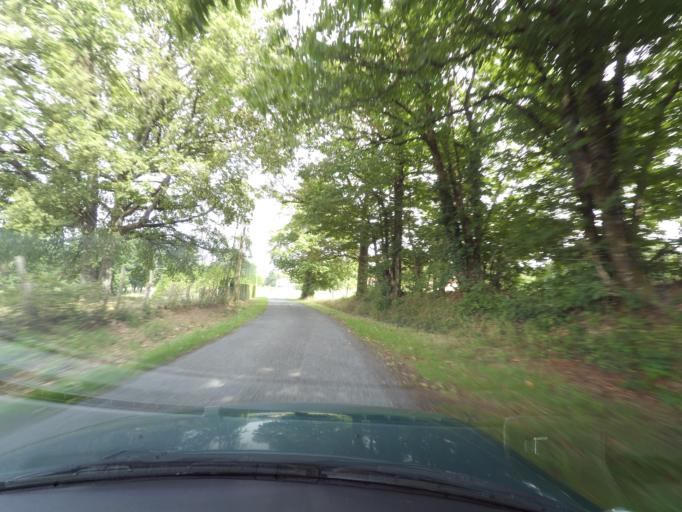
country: FR
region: Limousin
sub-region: Departement de la Haute-Vienne
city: Ladignac-le-Long
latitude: 45.6422
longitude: 1.1210
